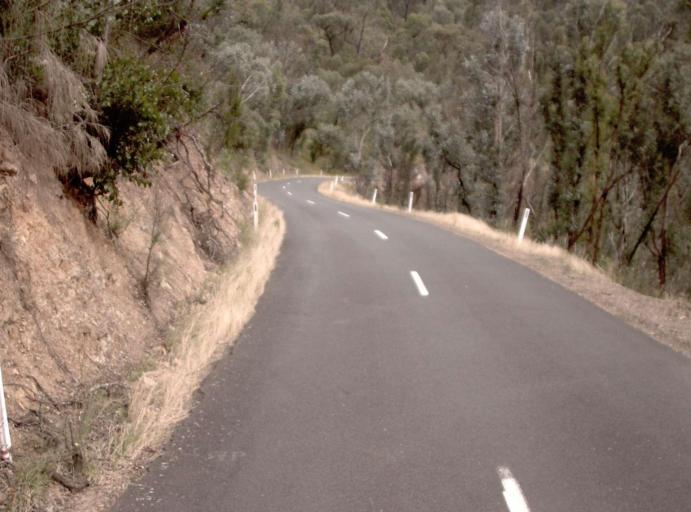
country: AU
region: Victoria
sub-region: Wellington
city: Heyfield
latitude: -37.7244
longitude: 146.6676
